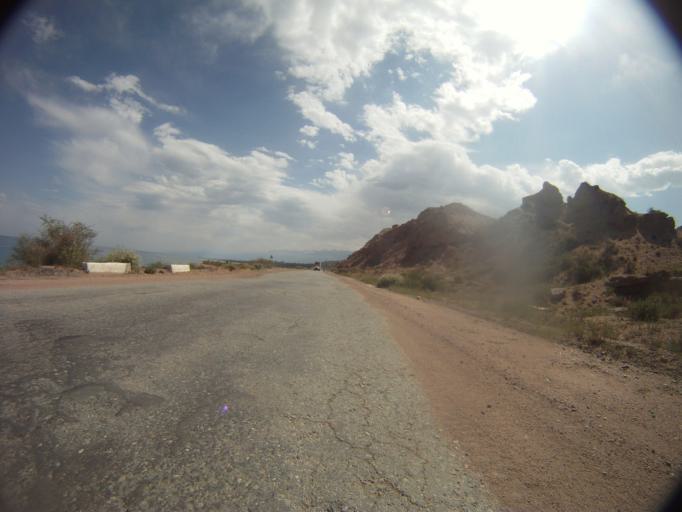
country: KG
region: Ysyk-Koel
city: Kadzhi-Say
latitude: 42.1741
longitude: 77.3545
